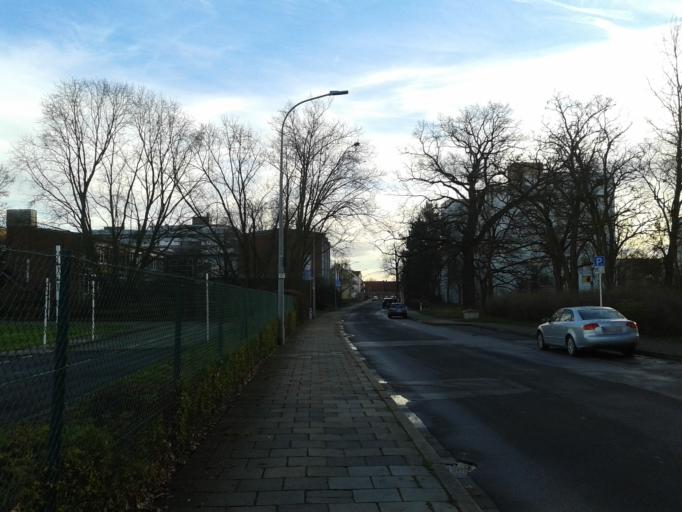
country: DE
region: Bavaria
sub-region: Upper Franconia
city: Bamberg
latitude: 49.9106
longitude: 10.9160
